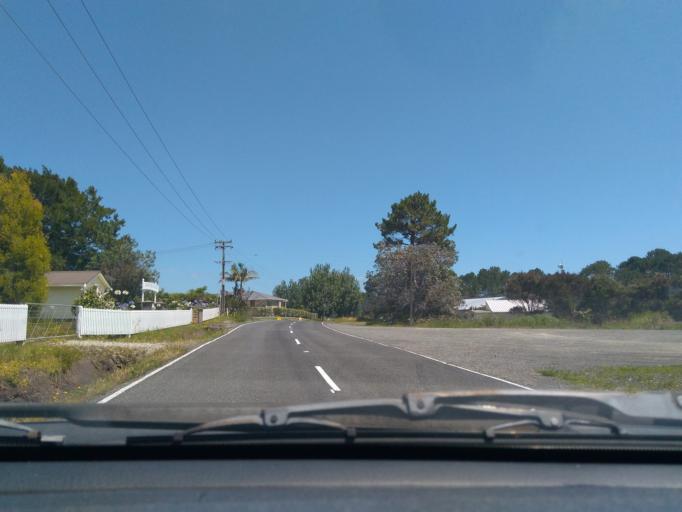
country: NZ
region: Northland
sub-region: Far North District
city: Taipa
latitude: -34.9943
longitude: 173.5239
